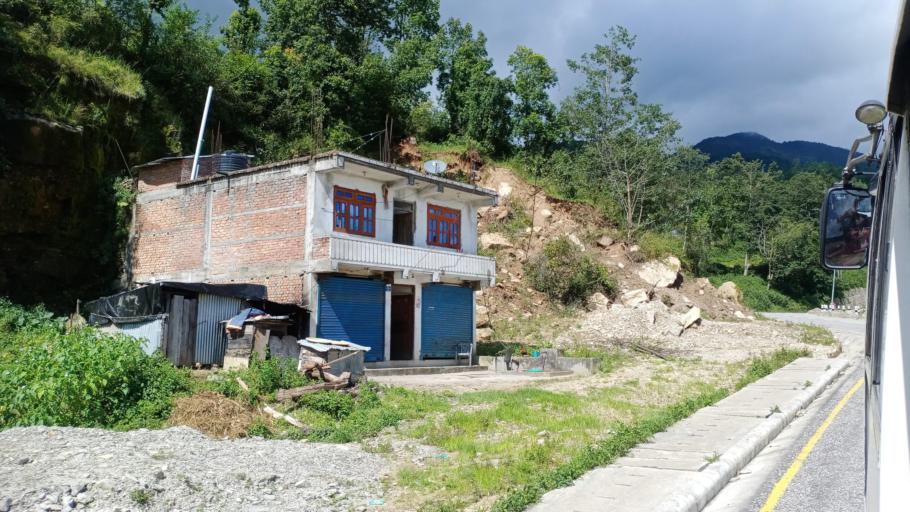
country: NP
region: Central Region
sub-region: Janakpur Zone
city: Ramechhap
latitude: 27.6491
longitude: 86.1404
